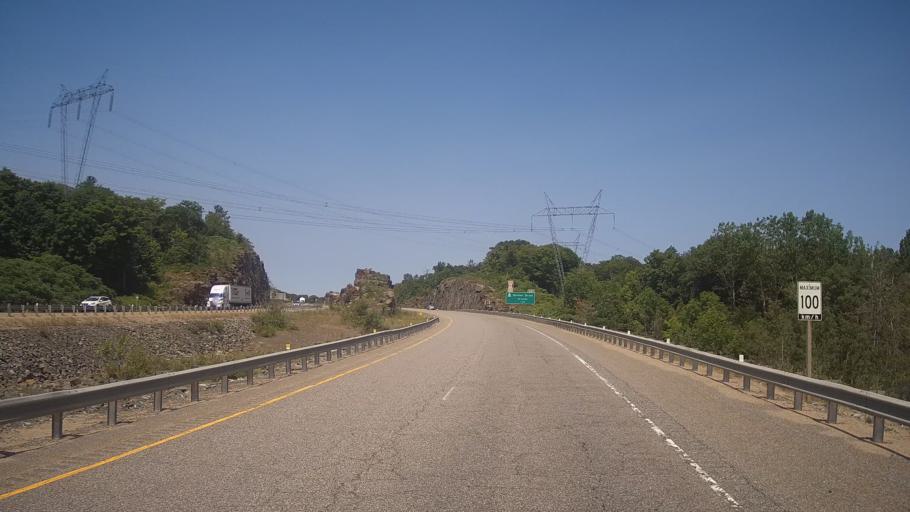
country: CA
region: Ontario
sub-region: Parry Sound District
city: Parry Sound
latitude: 45.3213
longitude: -79.9459
